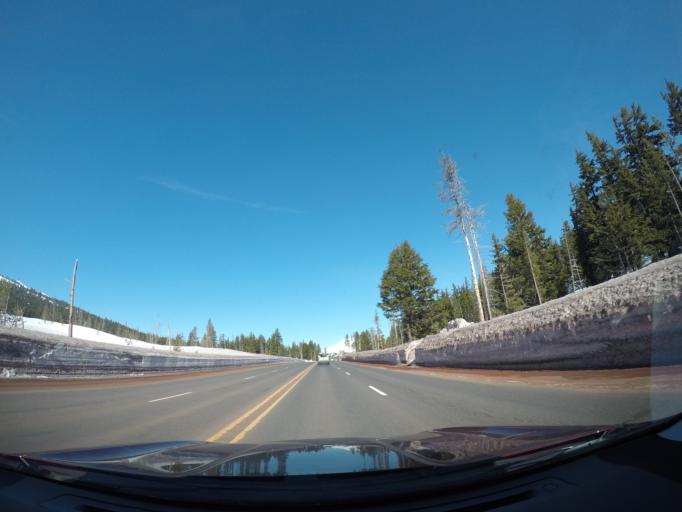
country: US
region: Oregon
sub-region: Deschutes County
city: Sunriver
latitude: 43.9934
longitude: -121.6581
